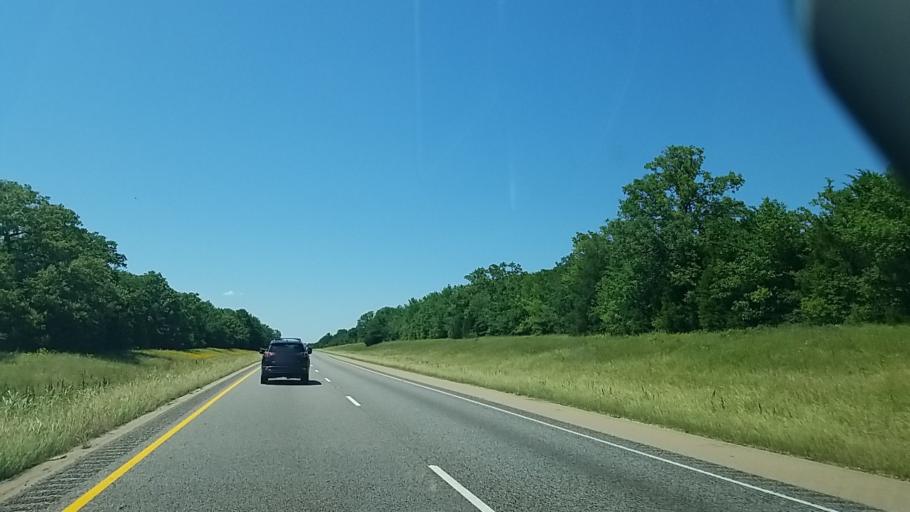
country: US
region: Texas
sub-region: Leon County
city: Buffalo
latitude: 31.5439
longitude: -96.1248
